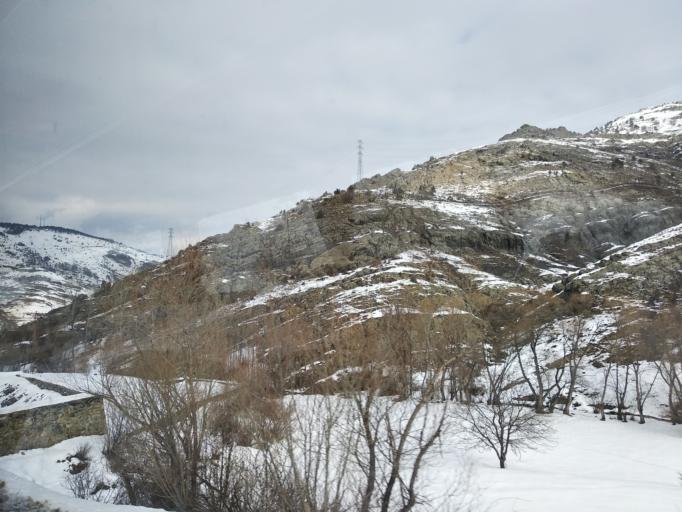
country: TR
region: Gumushane
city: Gumushkhane
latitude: 40.2910
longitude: 39.4816
